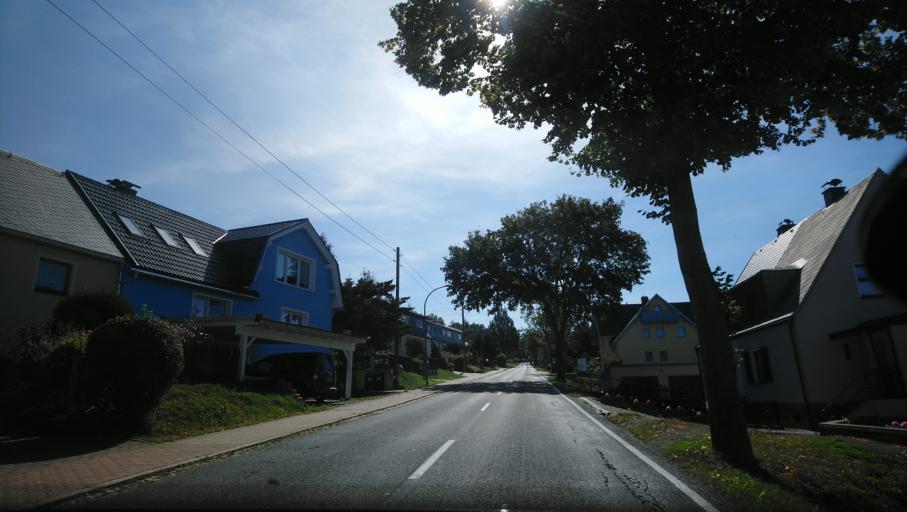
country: DE
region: Saxony
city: Konigswalde
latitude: 50.5402
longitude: 13.0546
